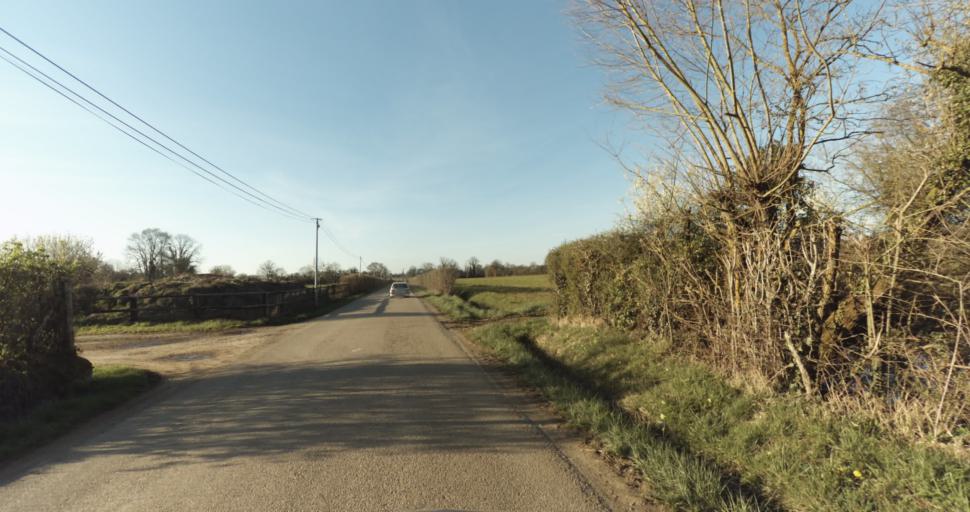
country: FR
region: Lower Normandy
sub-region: Departement du Calvados
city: Saint-Pierre-sur-Dives
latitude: 48.9794
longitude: -0.0098
